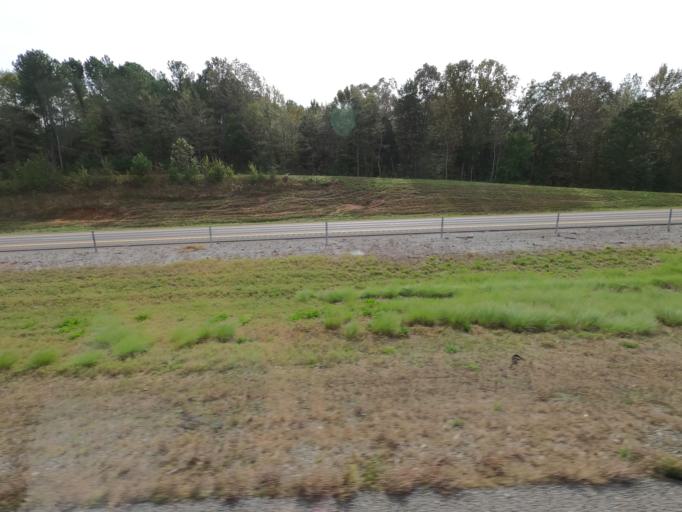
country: US
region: Tennessee
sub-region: Henderson County
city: Lexington
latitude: 35.8102
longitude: -88.3024
